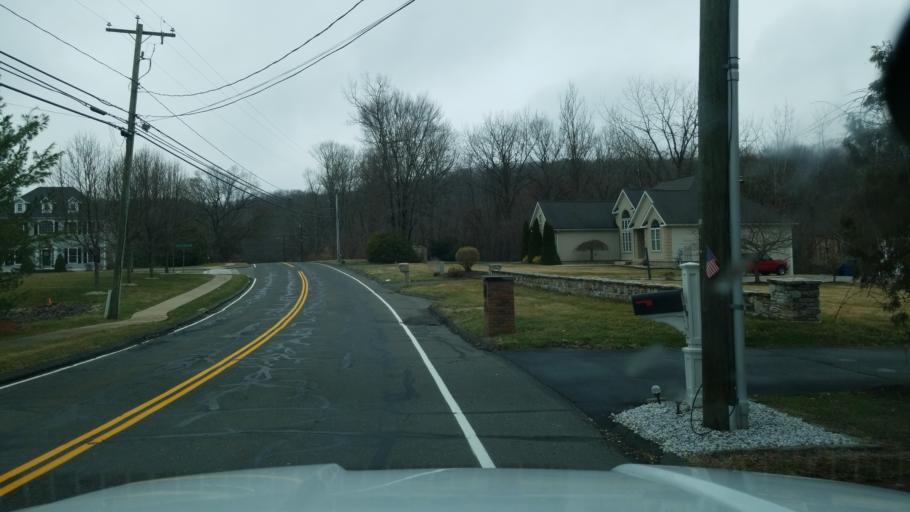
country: US
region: Connecticut
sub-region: Hartford County
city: Kensington
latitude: 41.6132
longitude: -72.7756
